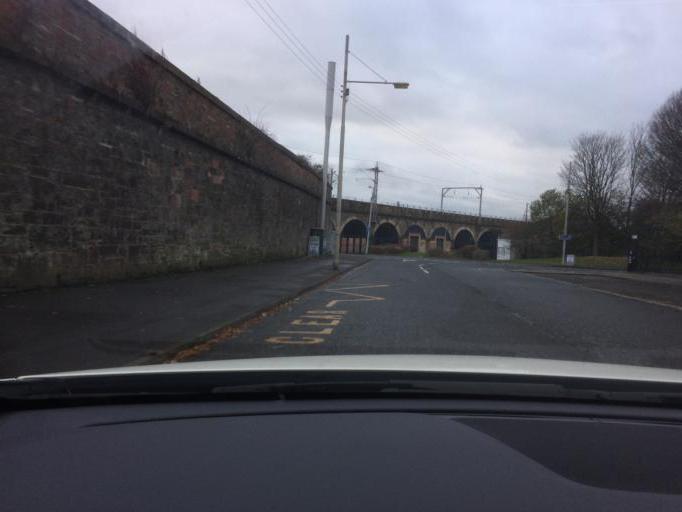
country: GB
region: Scotland
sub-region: Glasgow City
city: Glasgow
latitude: 55.8638
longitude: -4.2955
